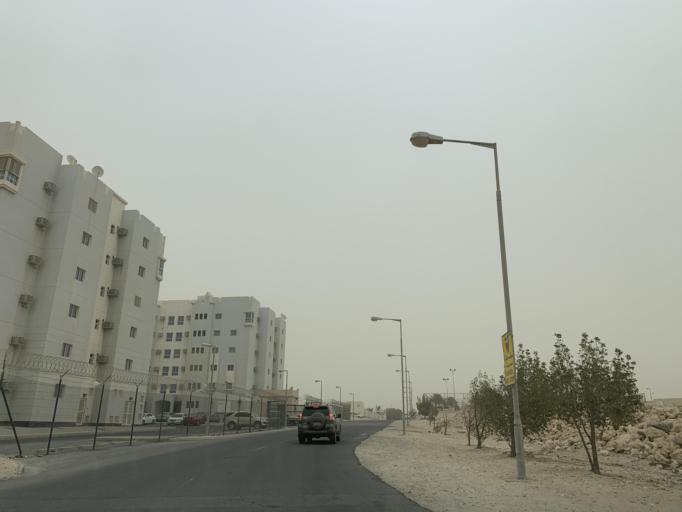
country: BH
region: Central Governorate
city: Madinat Hamad
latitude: 26.1333
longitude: 50.5221
